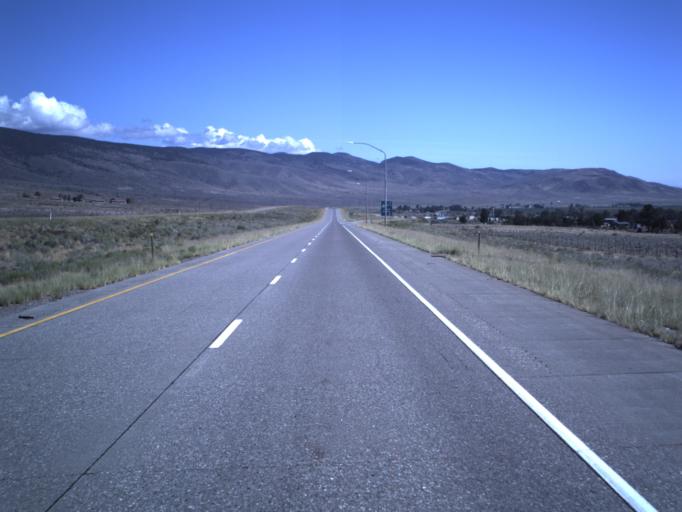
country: US
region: Utah
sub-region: Sevier County
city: Monroe
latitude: 38.6161
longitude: -112.2295
